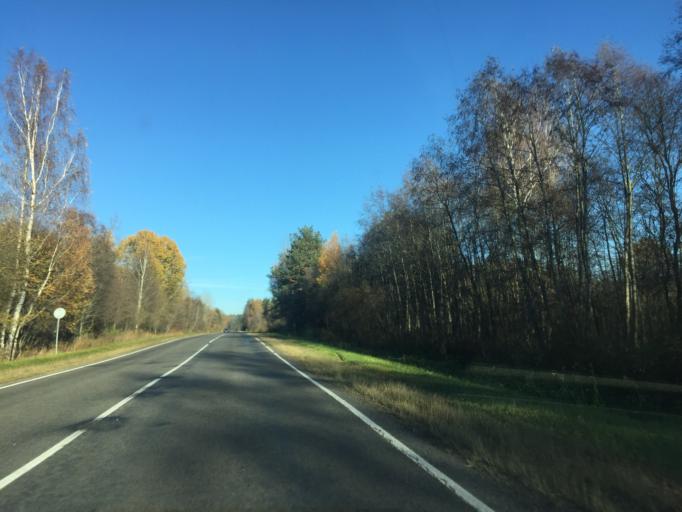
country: BY
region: Vitebsk
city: Dzisna
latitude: 55.3643
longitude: 28.3581
